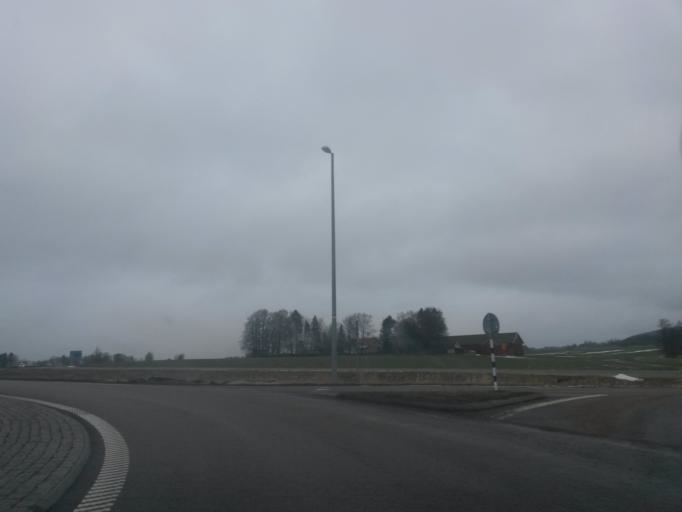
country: SE
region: Vaestra Goetaland
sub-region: Vanersborgs Kommun
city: Vargon
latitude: 58.2905
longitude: 12.3949
